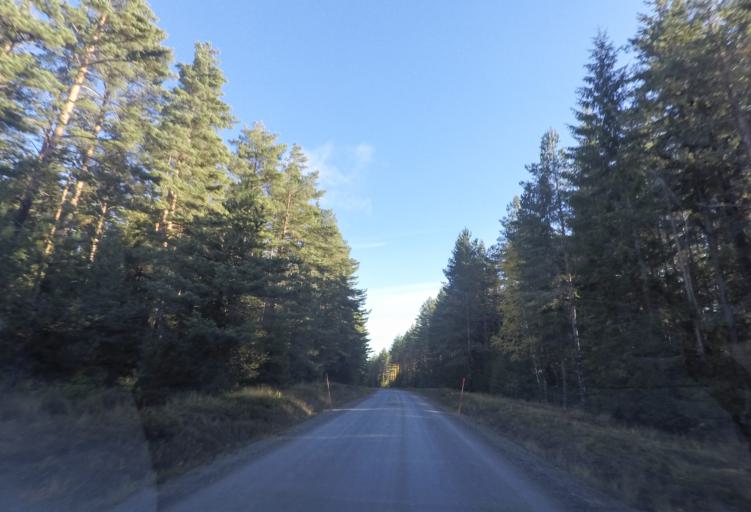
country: SE
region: OErebro
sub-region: Lindesbergs Kommun
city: Lindesberg
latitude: 59.6815
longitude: 15.3738
